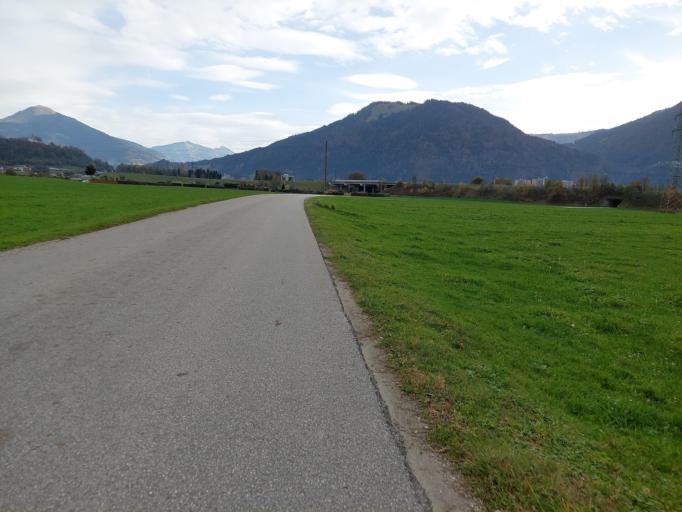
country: AT
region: Tyrol
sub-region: Politischer Bezirk Kufstein
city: Angath
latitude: 47.4995
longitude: 12.0667
